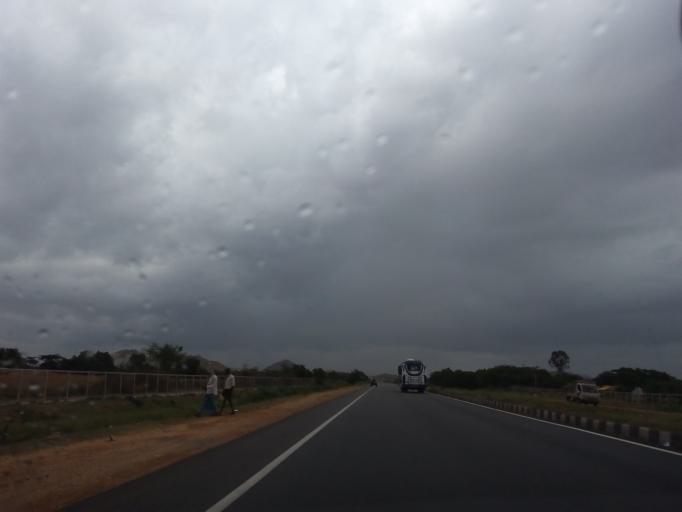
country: IN
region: Karnataka
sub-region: Chitradurga
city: Chitradurga
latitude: 14.2708
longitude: 76.3279
